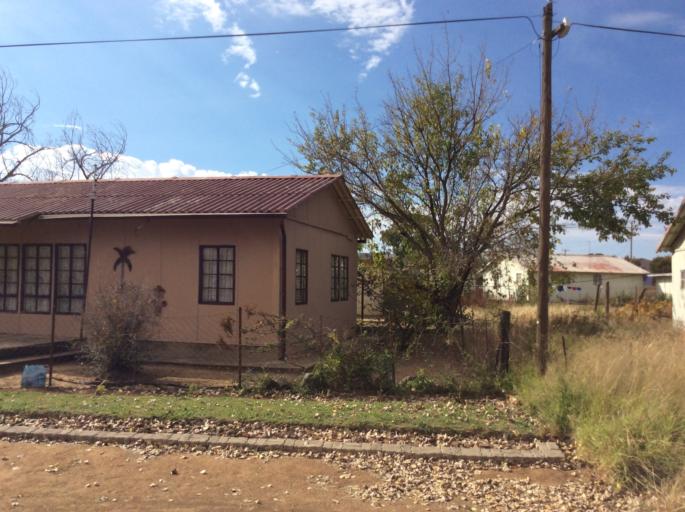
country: LS
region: Mafeteng
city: Mafeteng
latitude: -29.7288
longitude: 27.0251
